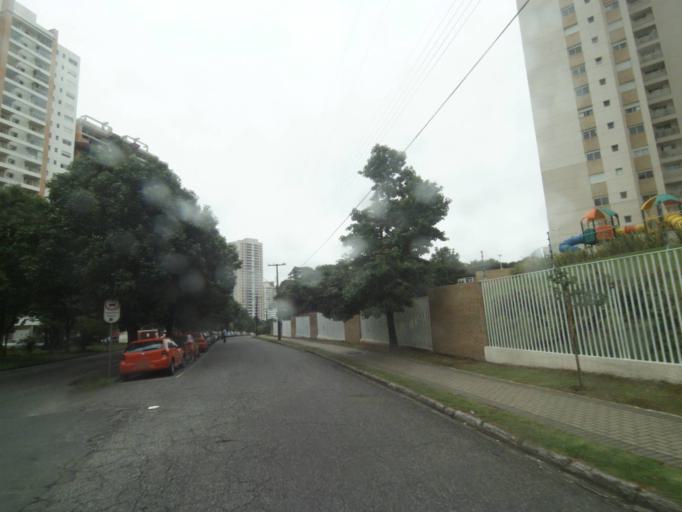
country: BR
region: Parana
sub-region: Curitiba
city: Curitiba
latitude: -25.4414
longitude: -49.3477
